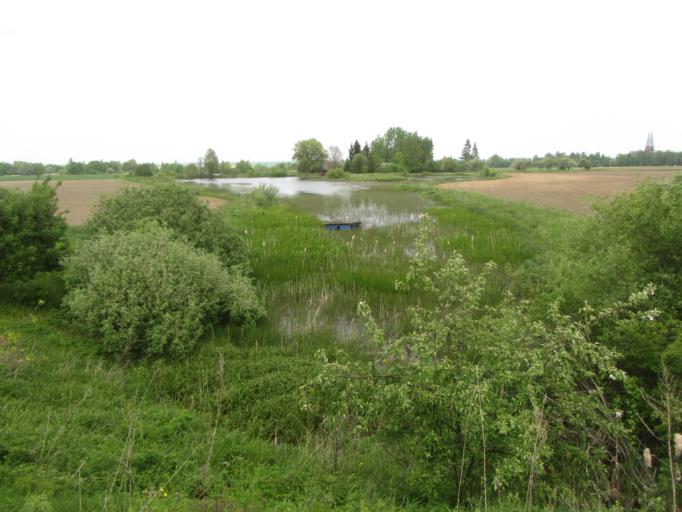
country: LT
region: Utenos apskritis
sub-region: Anyksciai
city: Anyksciai
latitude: 55.5772
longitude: 25.3088
